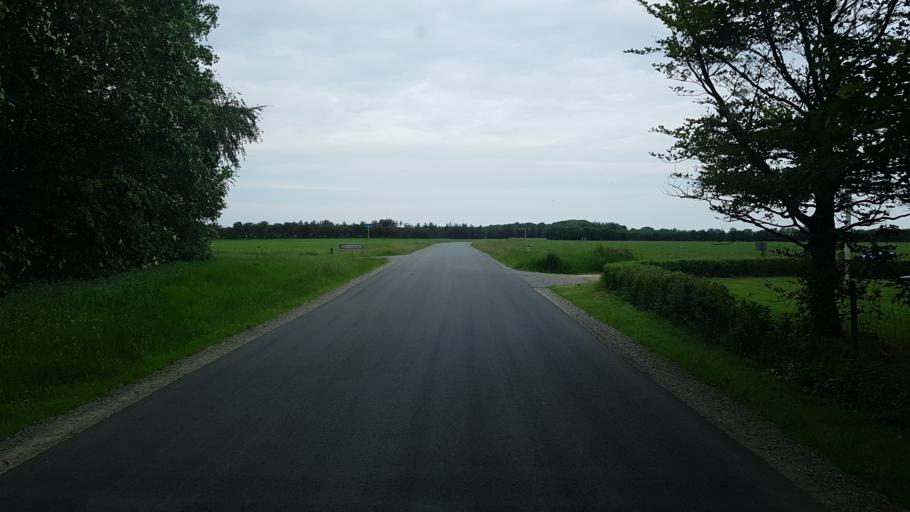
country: DK
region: South Denmark
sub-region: Varde Kommune
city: Oksbol
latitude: 55.7441
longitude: 8.3741
